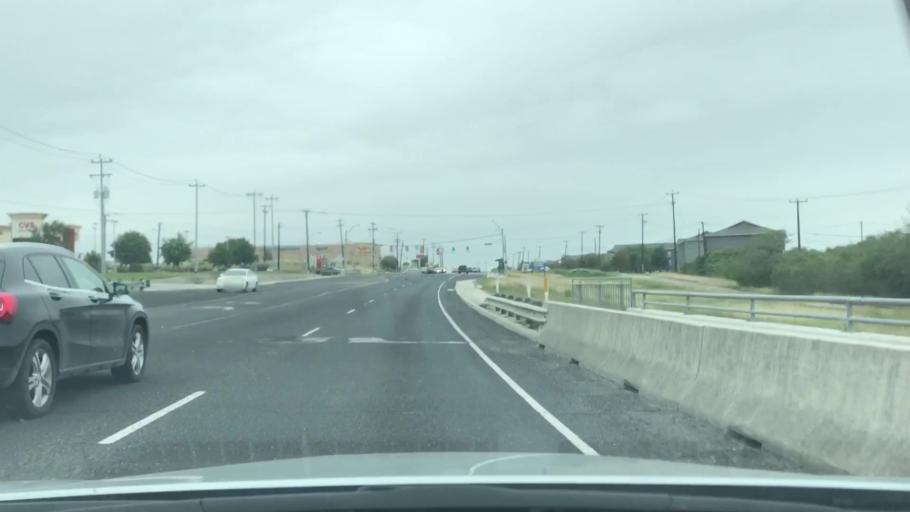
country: US
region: Texas
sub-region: Bexar County
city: Converse
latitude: 29.4861
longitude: -98.3454
